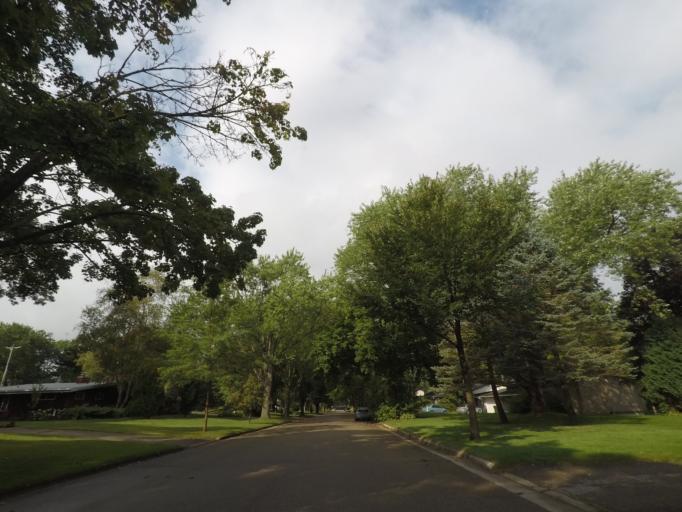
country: US
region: Wisconsin
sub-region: Dane County
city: Shorewood Hills
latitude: 43.0359
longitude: -89.4702
